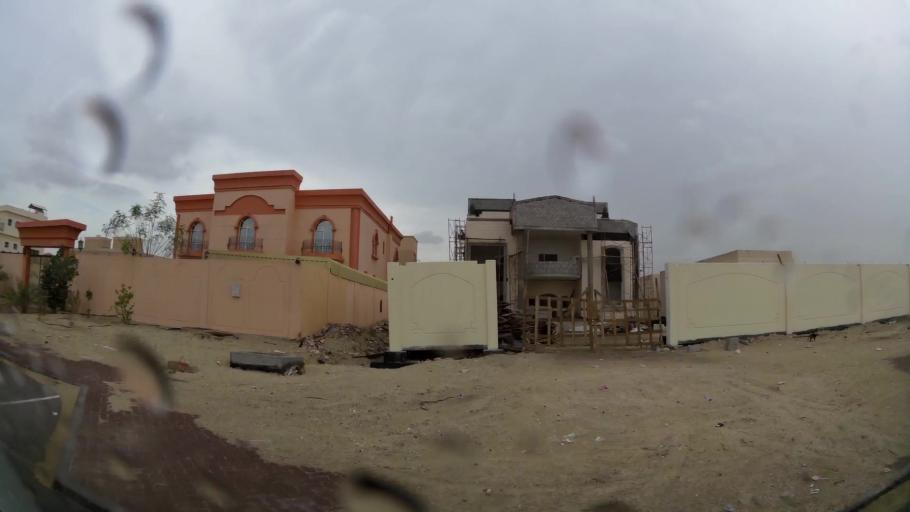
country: AE
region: Abu Dhabi
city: Abu Dhabi
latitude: 24.3653
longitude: 54.6419
